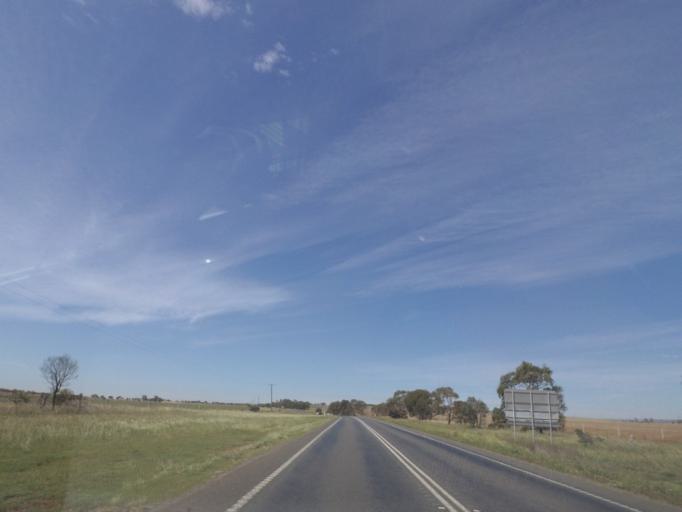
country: AU
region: Victoria
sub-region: Moorabool
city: Bacchus Marsh
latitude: -37.7544
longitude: 144.4425
